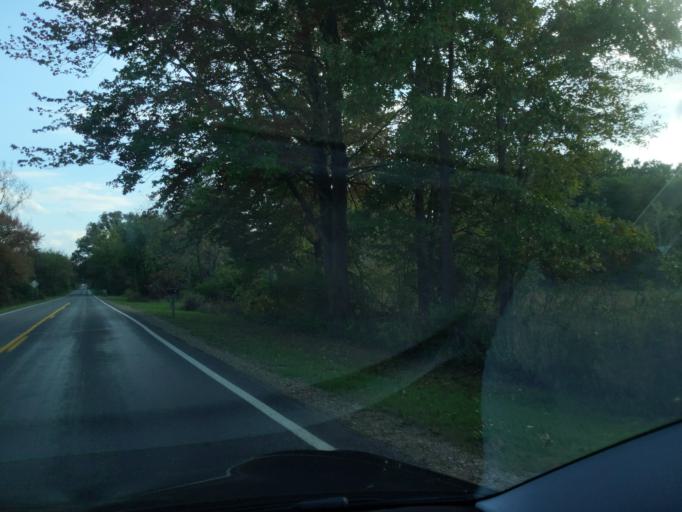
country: US
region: Michigan
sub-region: Jackson County
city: Jackson
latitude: 42.3211
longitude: -84.4628
